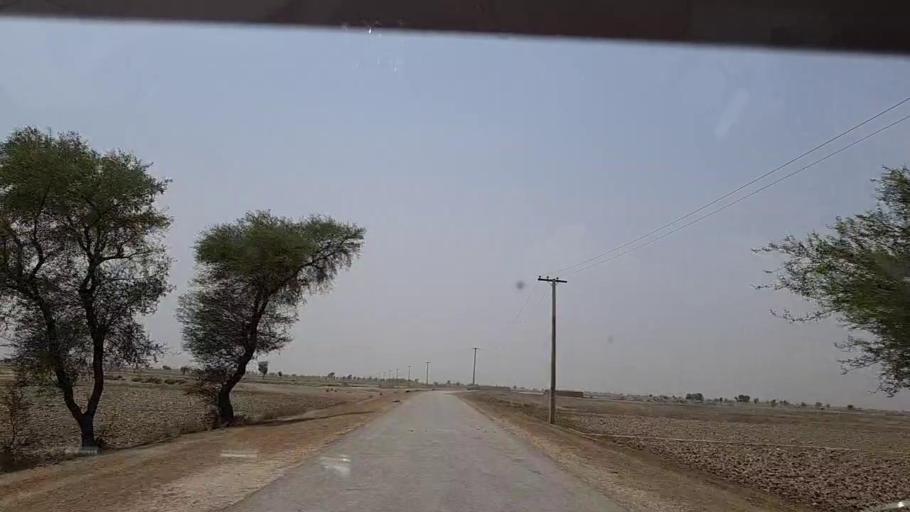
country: PK
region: Sindh
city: Phulji
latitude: 27.0059
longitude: 67.6253
